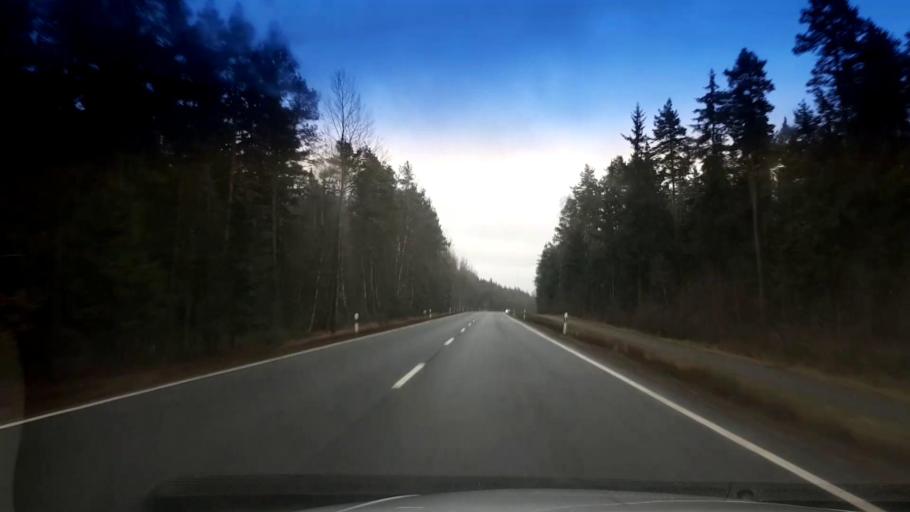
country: DE
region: Bavaria
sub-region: Upper Palatinate
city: Leonberg
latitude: 49.9139
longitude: 12.2965
